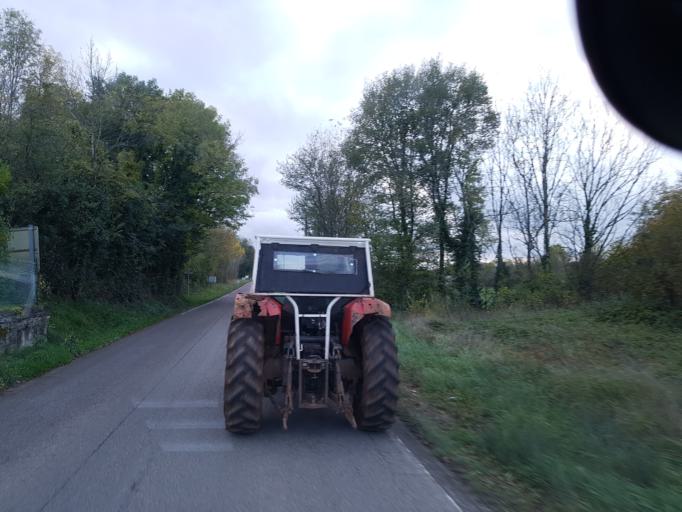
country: FR
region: Franche-Comte
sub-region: Departement du Jura
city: Arbois
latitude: 46.9159
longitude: 5.7550
